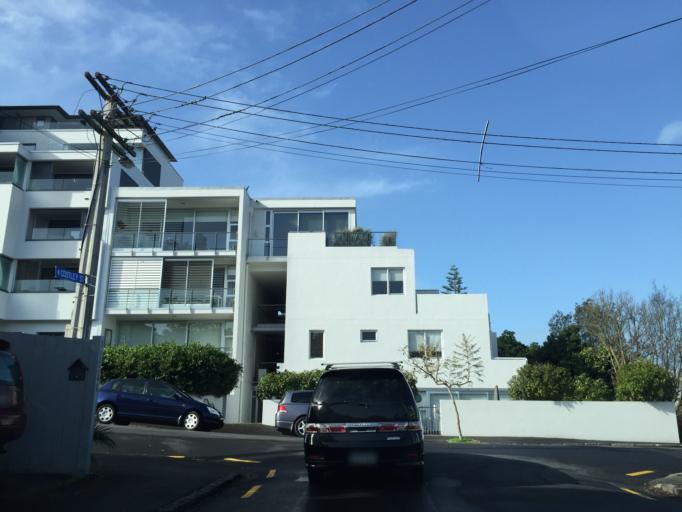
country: NZ
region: Auckland
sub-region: Auckland
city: Auckland
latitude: -36.8490
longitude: 174.7482
